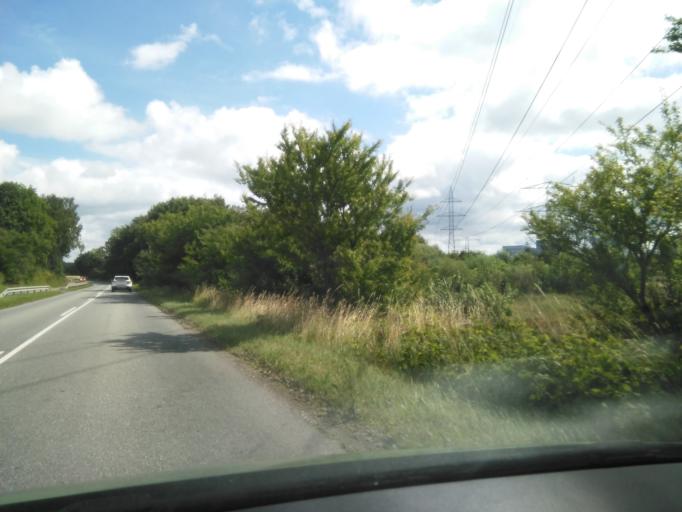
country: DK
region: Central Jutland
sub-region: Arhus Kommune
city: Logten
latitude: 56.2532
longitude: 10.3286
